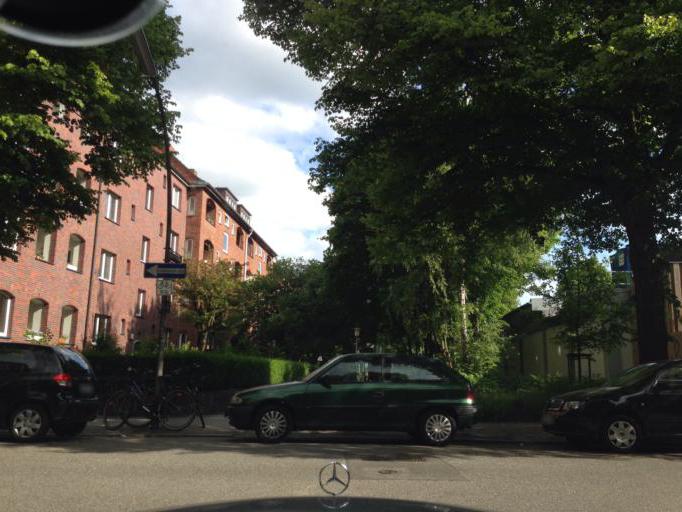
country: DE
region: Hamburg
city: Barmbek-Nord
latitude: 53.5800
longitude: 10.0514
